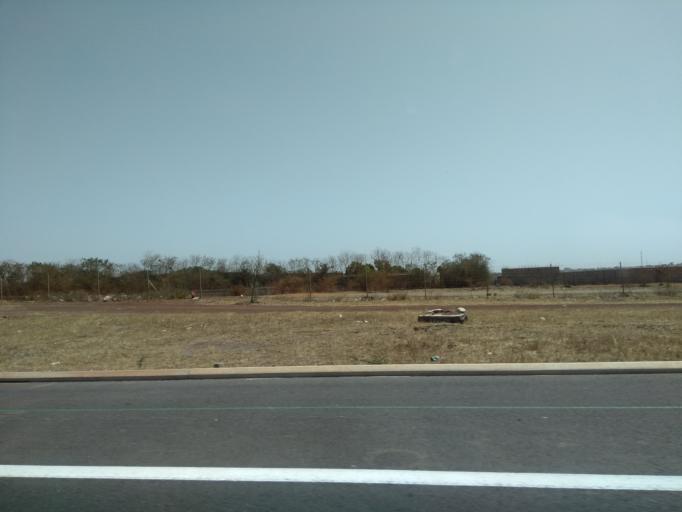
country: SN
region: Thies
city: Pout
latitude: 14.7352
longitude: -17.1760
